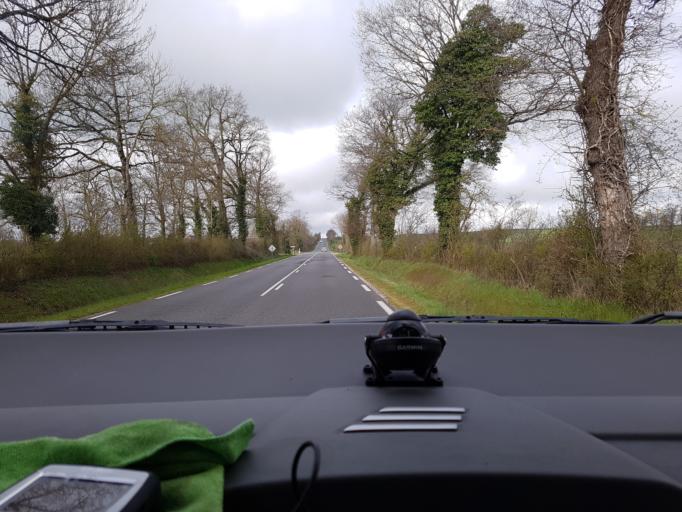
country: FR
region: Midi-Pyrenees
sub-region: Departement de l'Aveyron
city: Druelle
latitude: 44.3698
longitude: 2.4855
